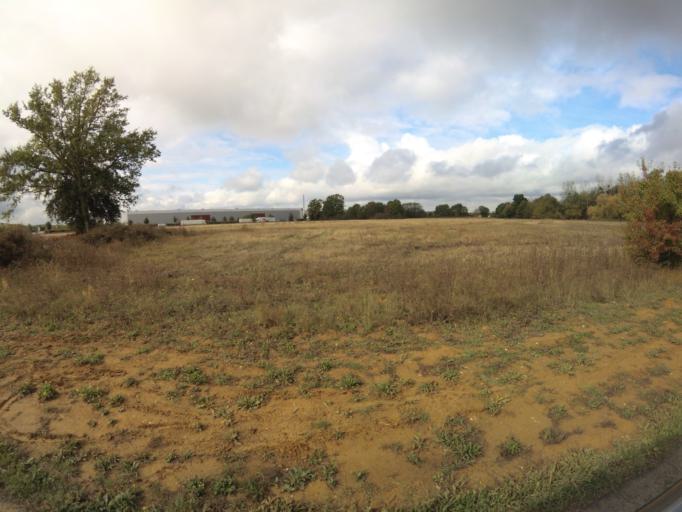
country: FR
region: Ile-de-France
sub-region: Departement de Seine-et-Marne
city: Montevrain
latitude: 48.8624
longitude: 2.7533
